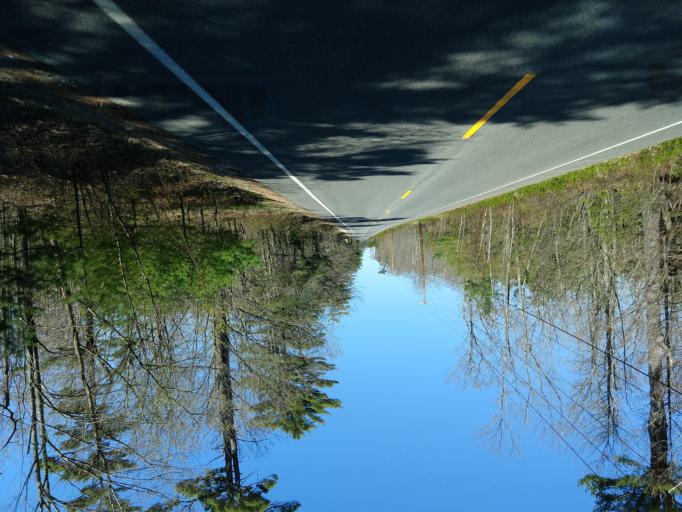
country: US
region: Maine
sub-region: York County
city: Kennebunk
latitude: 43.3506
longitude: -70.5281
